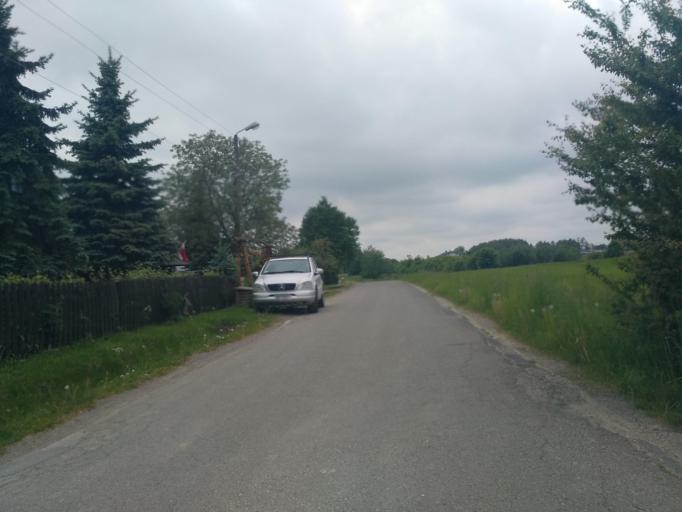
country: PL
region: Subcarpathian Voivodeship
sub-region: Krosno
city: Krosno
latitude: 49.6721
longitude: 21.7423
